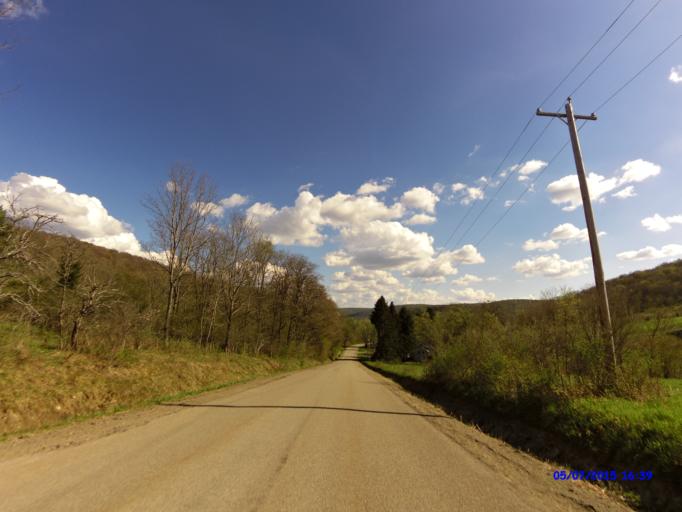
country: US
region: New York
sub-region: Cattaraugus County
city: Little Valley
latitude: 42.2996
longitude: -78.6785
